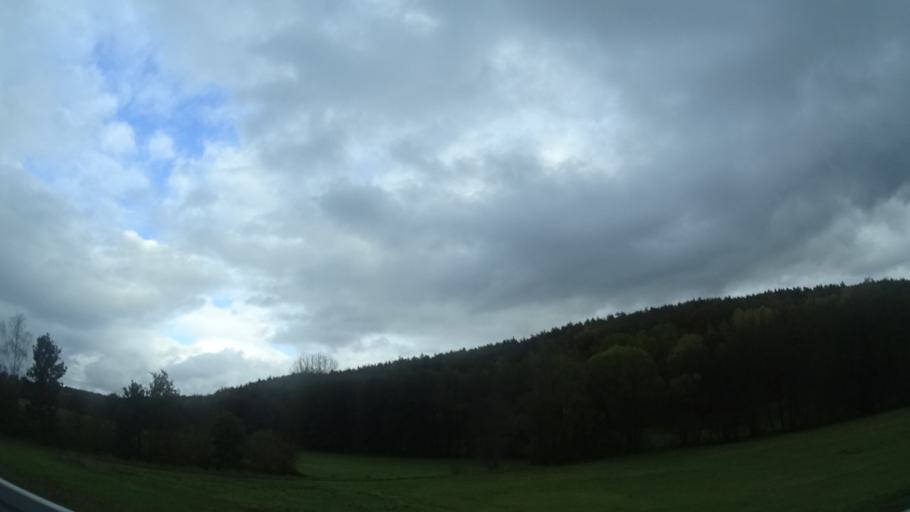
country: DE
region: Bavaria
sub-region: Regierungsbezirk Unterfranken
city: Oberelsbach
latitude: 50.3948
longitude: 10.0919
